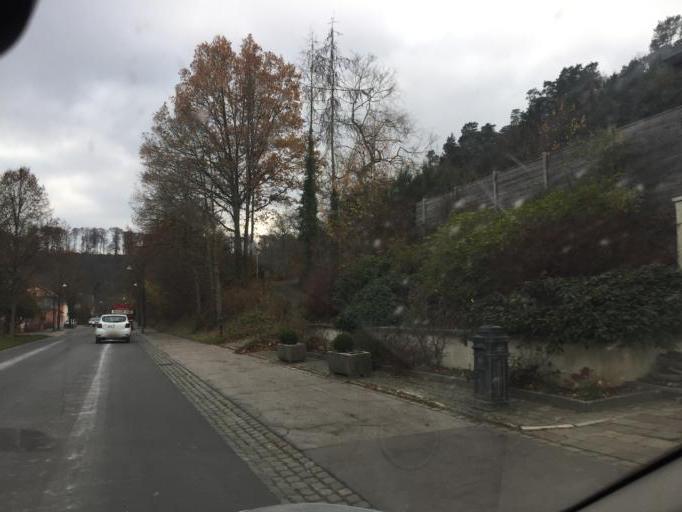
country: LU
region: Diekirch
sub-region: Canton de Redange
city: Saeul
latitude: 49.7300
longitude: 5.9836
